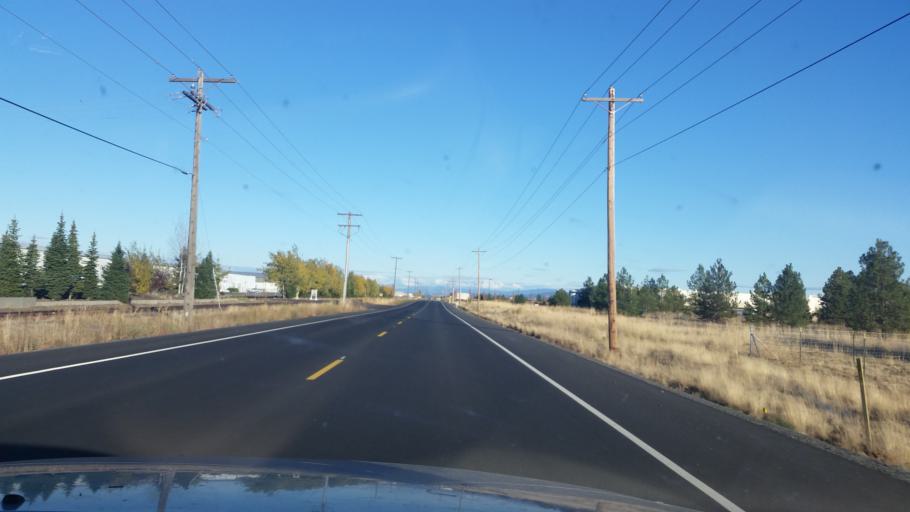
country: US
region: Washington
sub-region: Spokane County
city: Airway Heights
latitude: 47.6283
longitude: -117.5938
